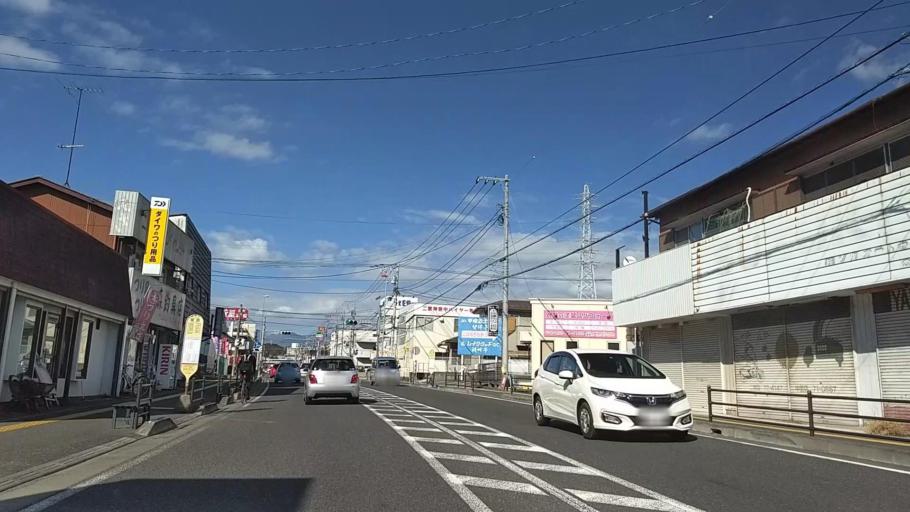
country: JP
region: Kanagawa
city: Ninomiya
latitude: 35.3054
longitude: 139.2552
